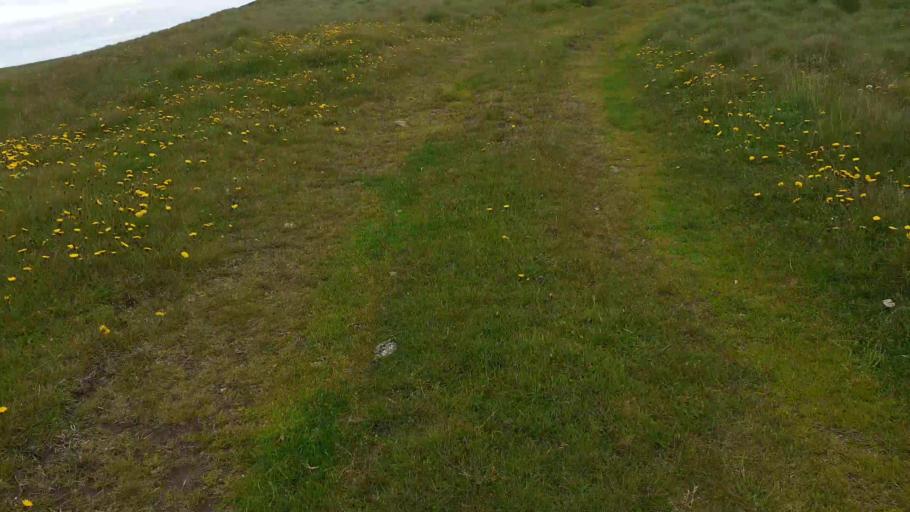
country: IS
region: Northeast
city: Dalvik
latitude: 66.5423
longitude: -17.9840
